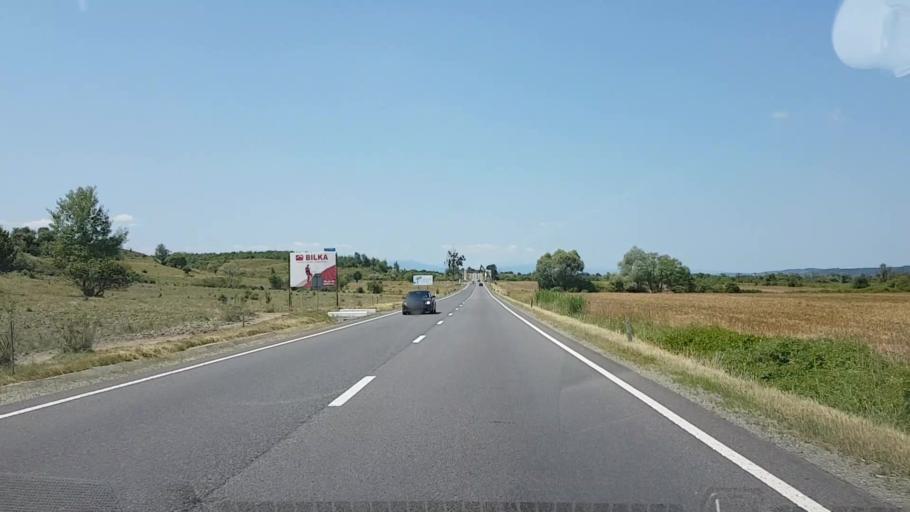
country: RO
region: Brasov
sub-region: Comuna Ucea de Jos
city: Ucea de Jos
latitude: 45.7855
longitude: 24.6488
